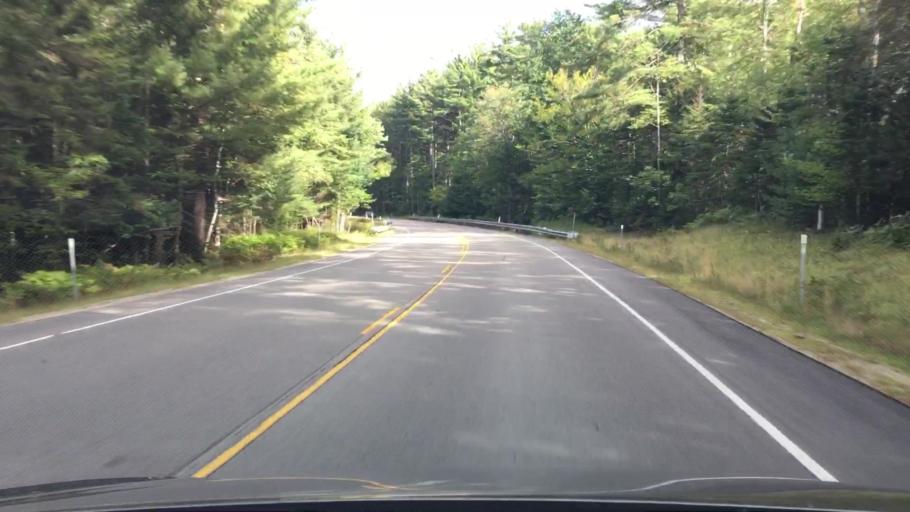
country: US
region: New Hampshire
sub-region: Carroll County
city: Tamworth
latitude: 43.9891
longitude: -71.3166
